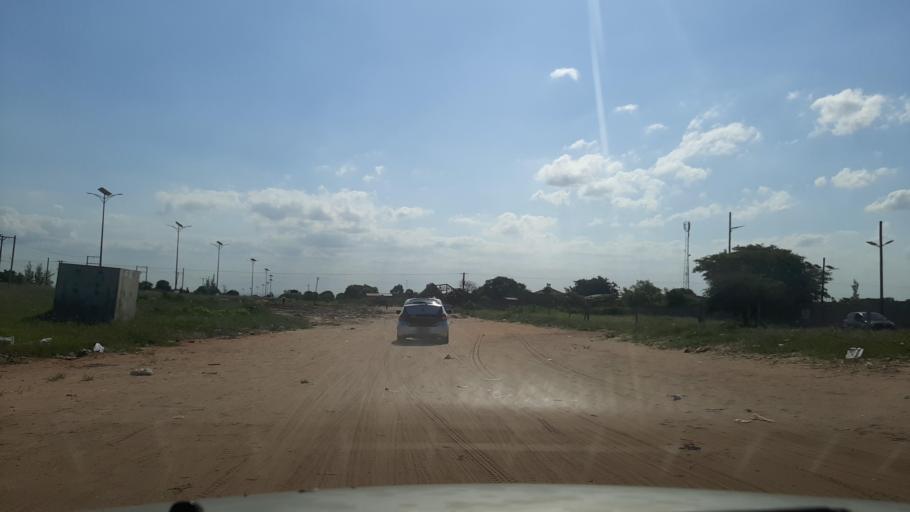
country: MZ
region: Maputo
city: Matola
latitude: -25.8153
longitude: 32.4934
